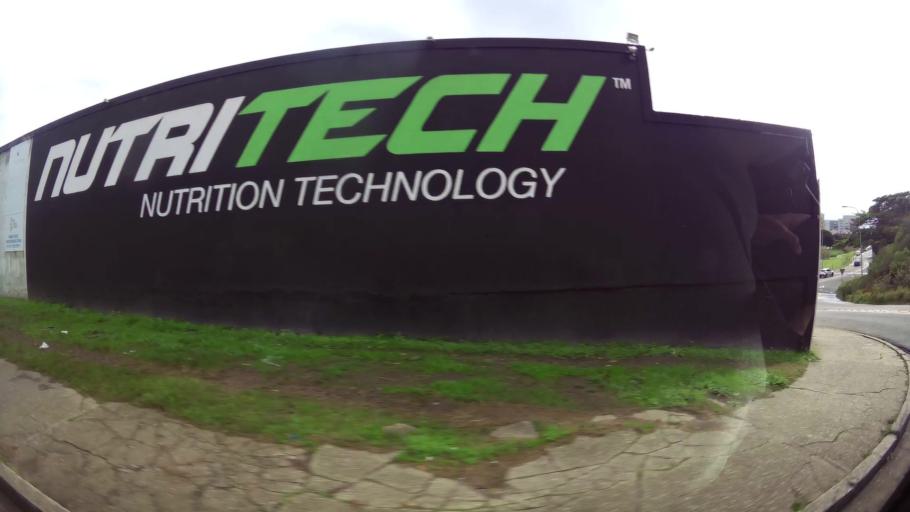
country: ZA
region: Eastern Cape
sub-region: Nelson Mandela Bay Metropolitan Municipality
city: Port Elizabeth
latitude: -33.9682
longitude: 25.6227
